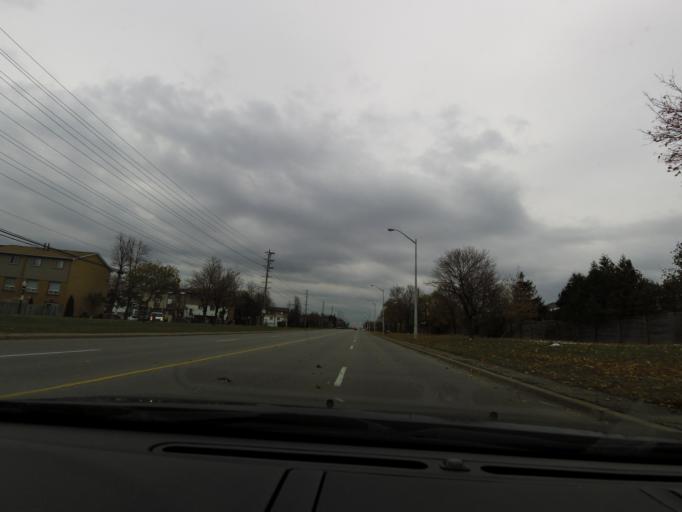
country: CA
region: Ontario
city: Brampton
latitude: 43.7319
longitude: -79.7511
